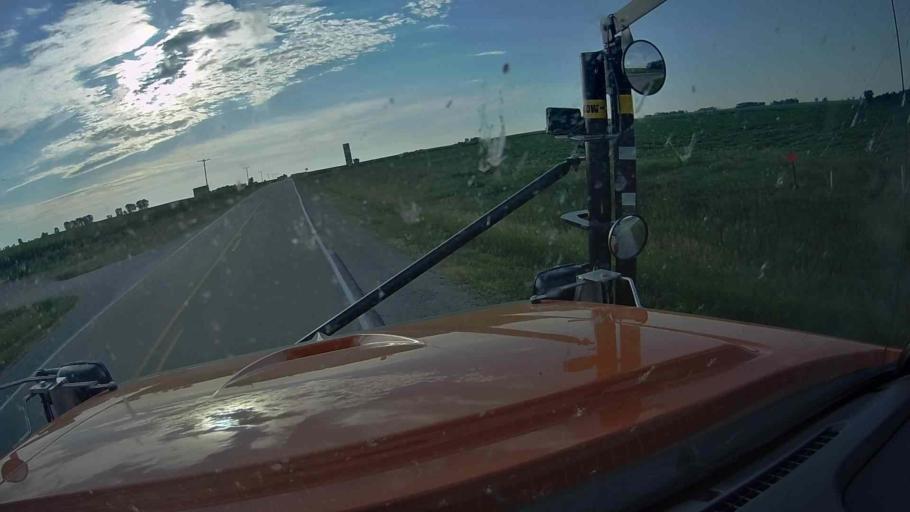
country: US
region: Iowa
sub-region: Cerro Gordo County
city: Rockwell
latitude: 43.0667
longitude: -93.2011
